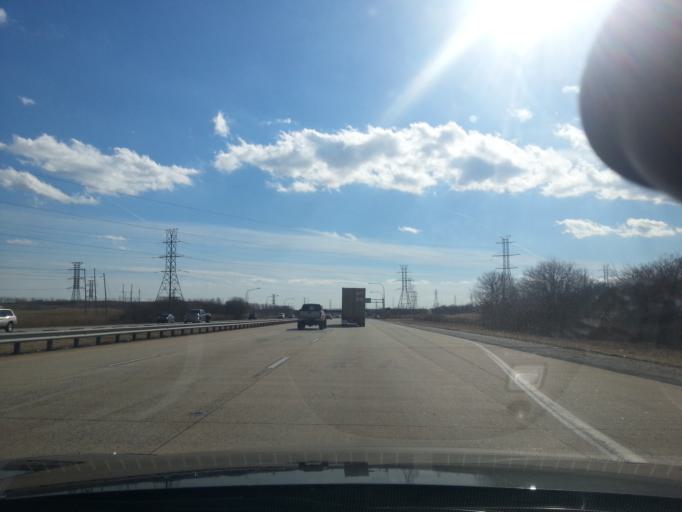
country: US
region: Delaware
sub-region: New Castle County
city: Edgemoor
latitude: 39.7403
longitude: -75.5177
